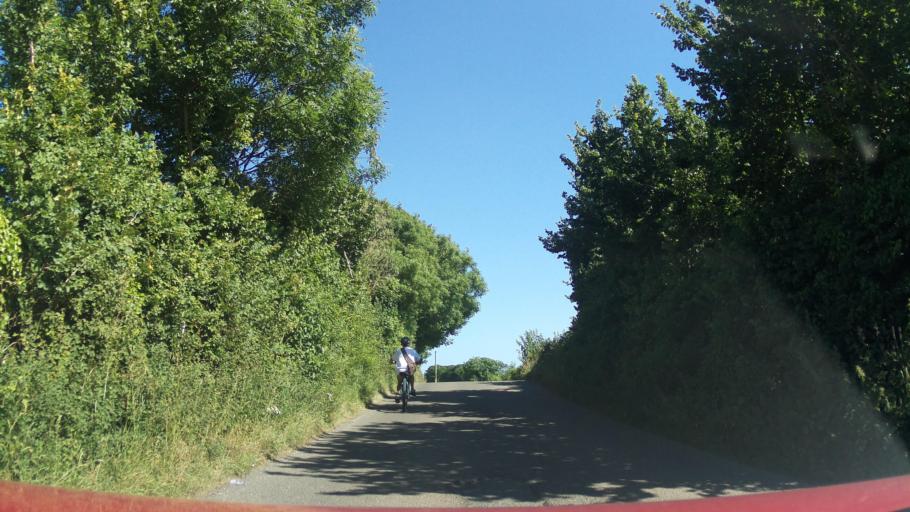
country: GB
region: England
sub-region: Borough of Torbay
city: Brixham
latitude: 50.3957
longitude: -3.5405
